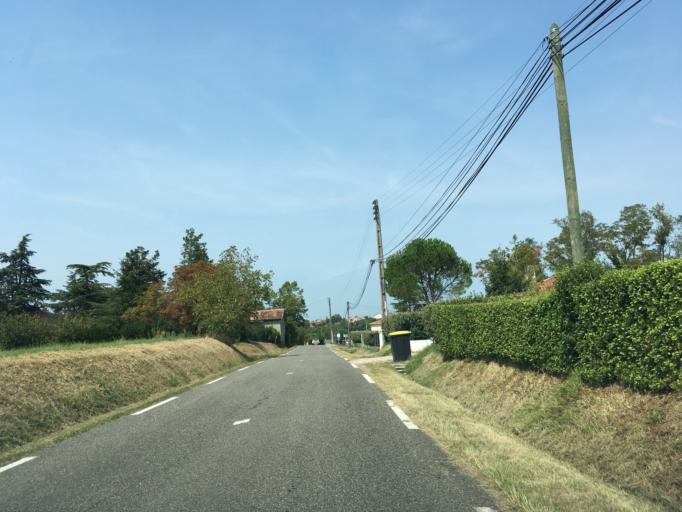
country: FR
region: Midi-Pyrenees
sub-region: Departement du Tarn-et-Garonne
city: Corbarieu
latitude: 43.9560
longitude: 1.3921
